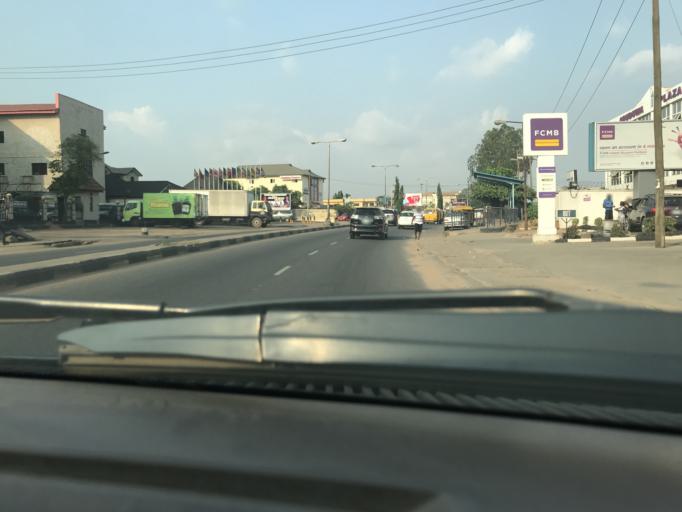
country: NG
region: Lagos
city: Ikotun
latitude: 6.5840
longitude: 3.2837
